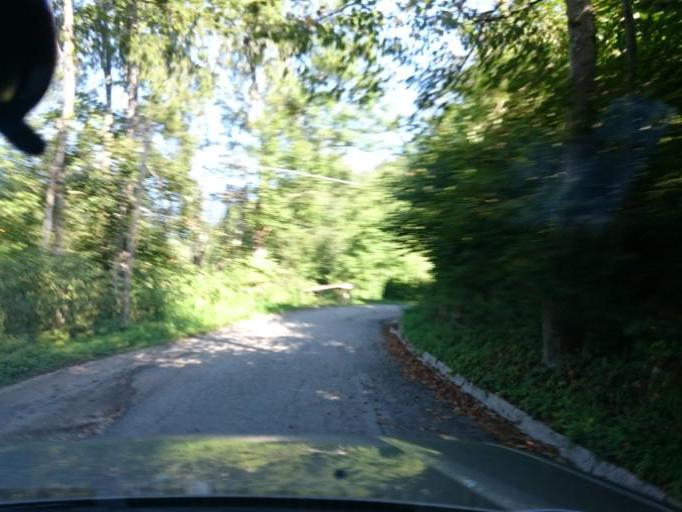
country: IT
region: Friuli Venezia Giulia
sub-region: Provincia di Udine
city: Tarvisio
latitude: 46.4937
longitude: 13.6397
